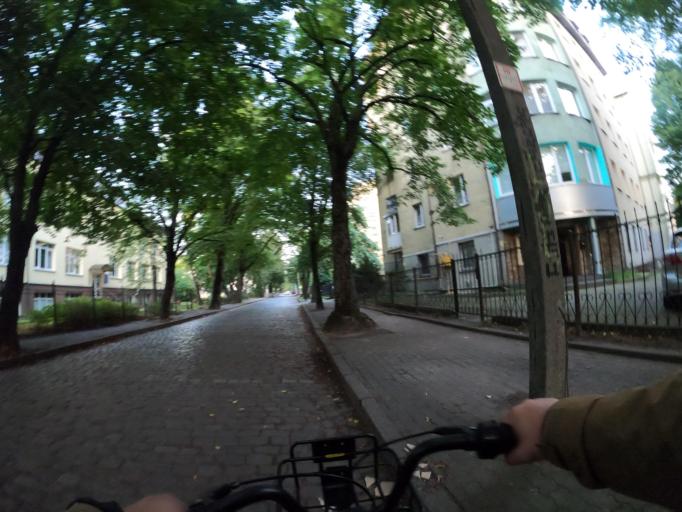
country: RU
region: Kaliningrad
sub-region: Gorod Kaliningrad
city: Kaliningrad
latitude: 54.7254
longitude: 20.4768
